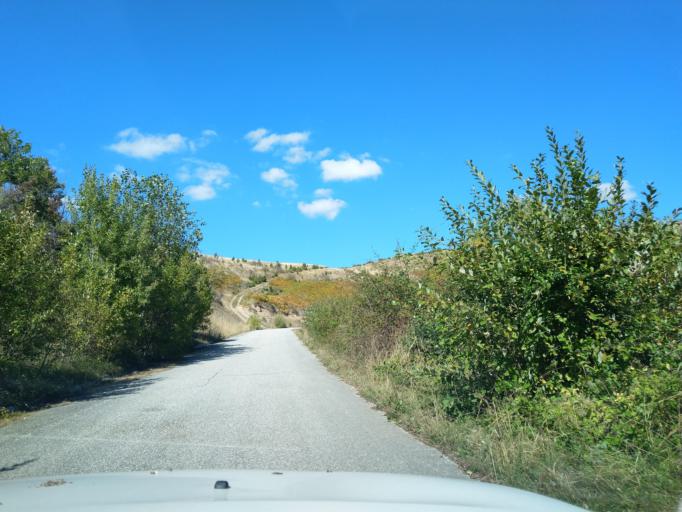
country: RS
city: Sokolovica
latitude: 43.2530
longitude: 20.3324
